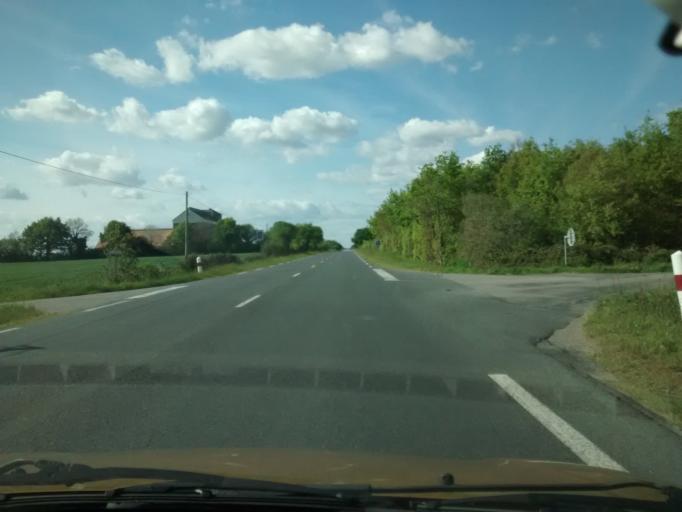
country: FR
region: Pays de la Loire
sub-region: Departement de la Loire-Atlantique
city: Geneston
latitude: 47.0782
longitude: -1.5236
